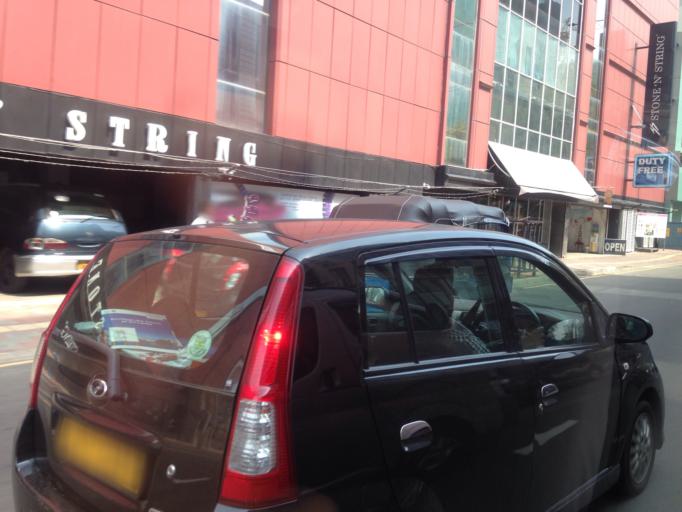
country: LK
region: Western
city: Colombo
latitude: 6.9085
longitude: 79.8527
